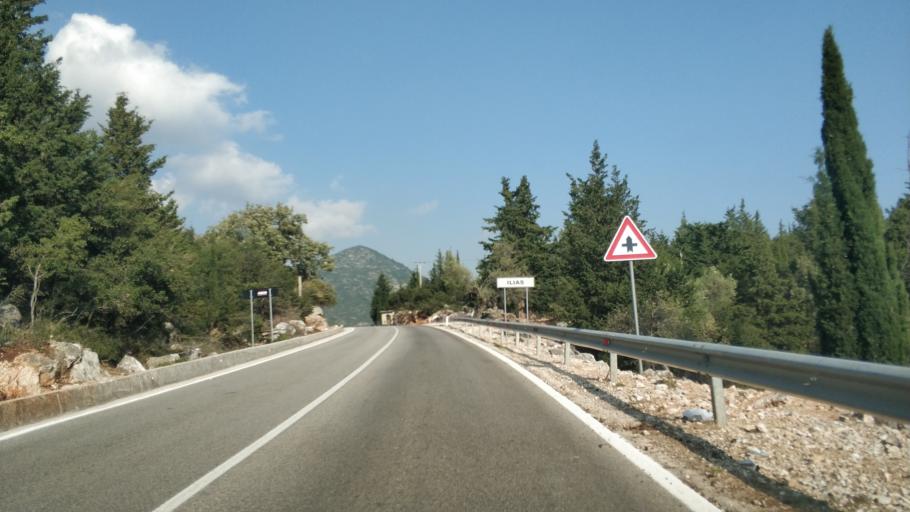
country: AL
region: Vlore
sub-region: Rrethi i Vlores
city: Vranisht
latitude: 40.1418
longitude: 19.6694
